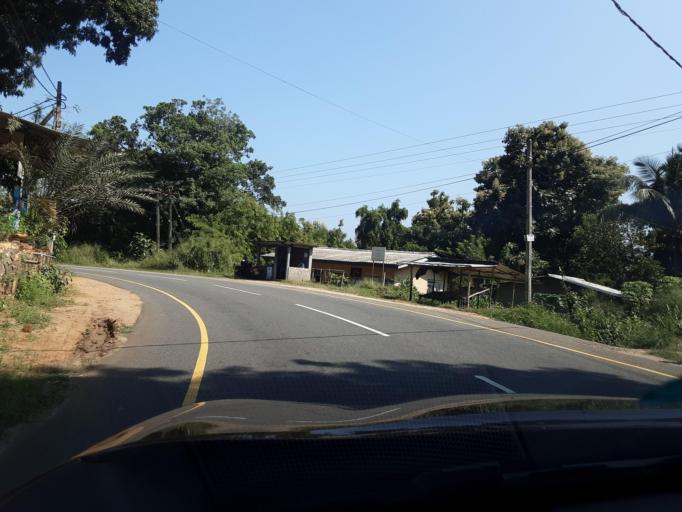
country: LK
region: Uva
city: Badulla
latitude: 7.1655
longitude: 81.0527
